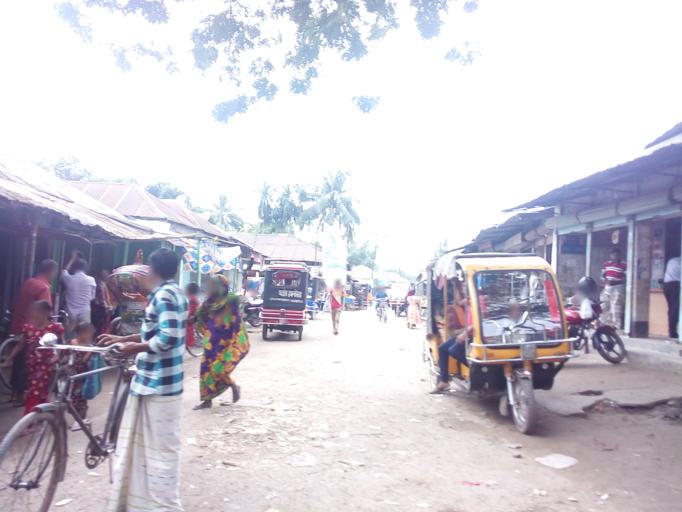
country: BD
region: Rangpur Division
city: Nageswari
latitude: 25.8906
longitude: 89.7098
